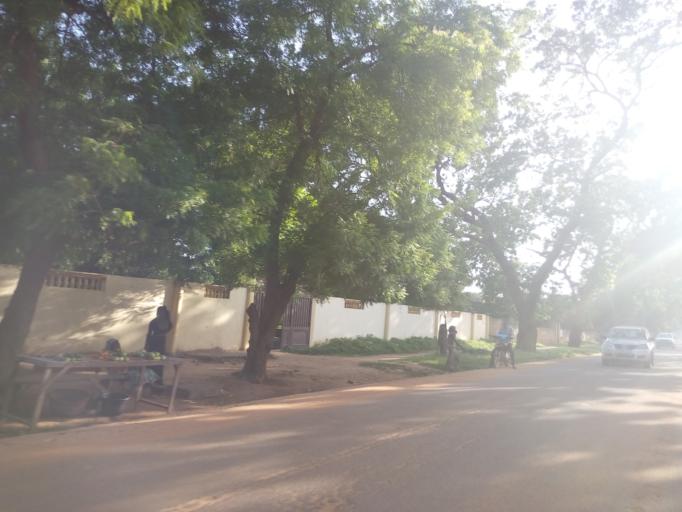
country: ML
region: Segou
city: Segou
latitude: 13.4429
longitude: -6.2709
